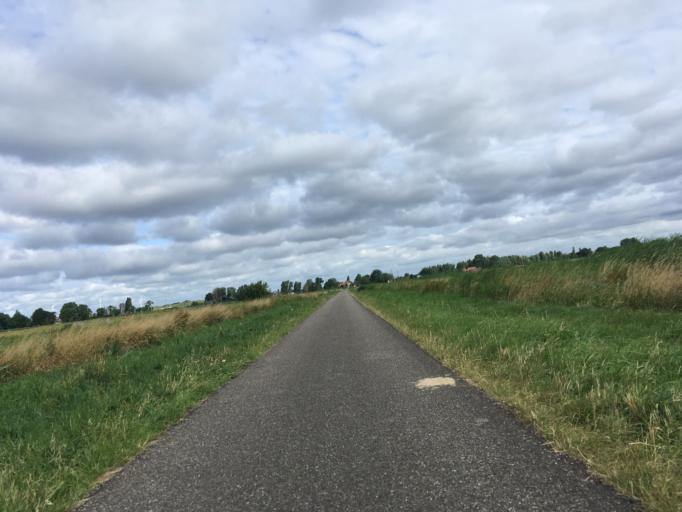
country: NL
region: North Holland
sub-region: Gemeente Haarlem
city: Haarlem
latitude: 52.3973
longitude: 4.6878
